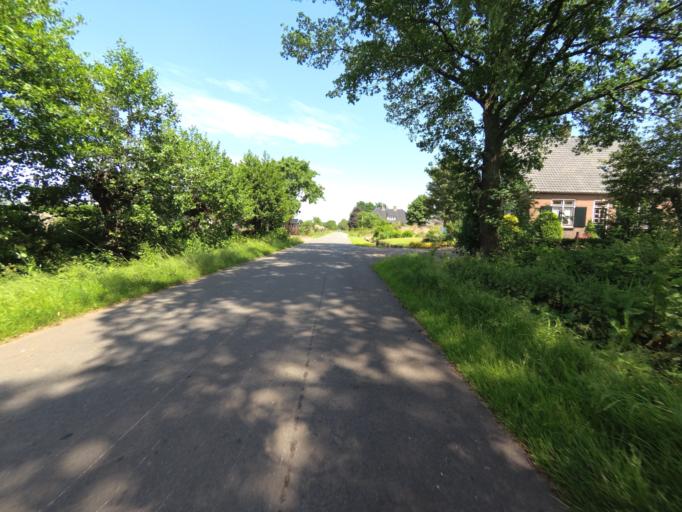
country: NL
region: Gelderland
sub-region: Gemeente Ede
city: Lunteren
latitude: 52.0614
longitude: 5.6314
